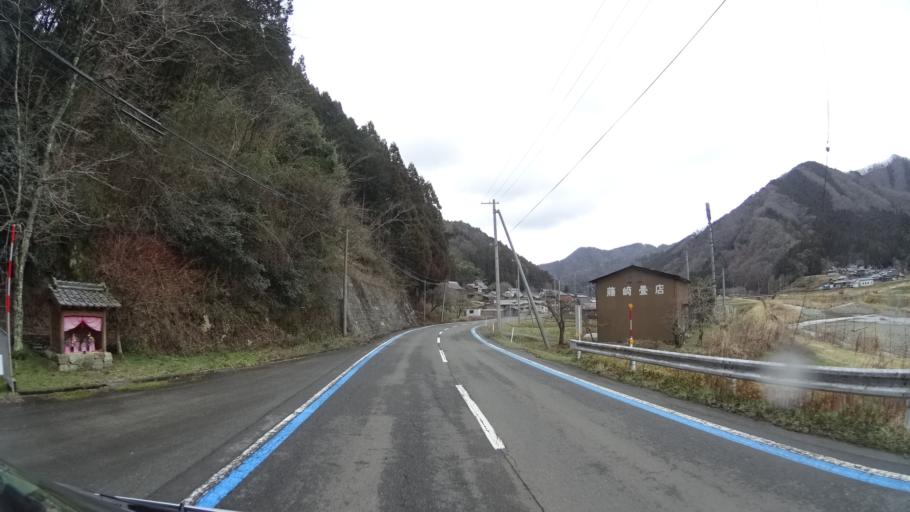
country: JP
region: Kyoto
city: Maizuru
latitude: 35.3949
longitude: 135.4131
